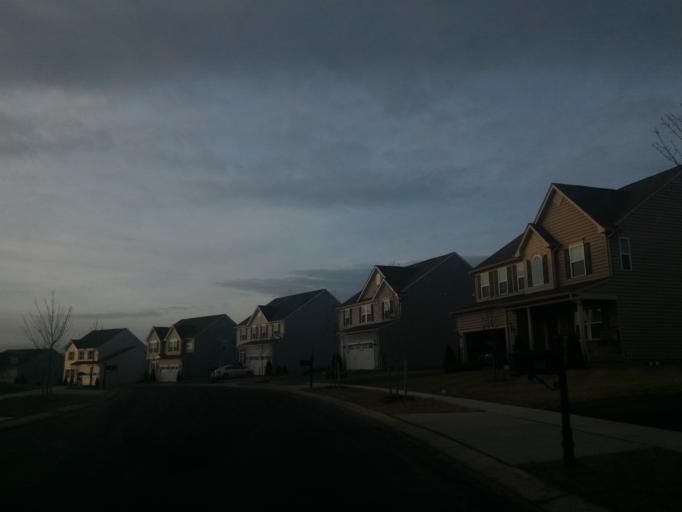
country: US
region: Pennsylvania
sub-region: York County
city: Loganville
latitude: 39.8623
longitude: -76.7259
